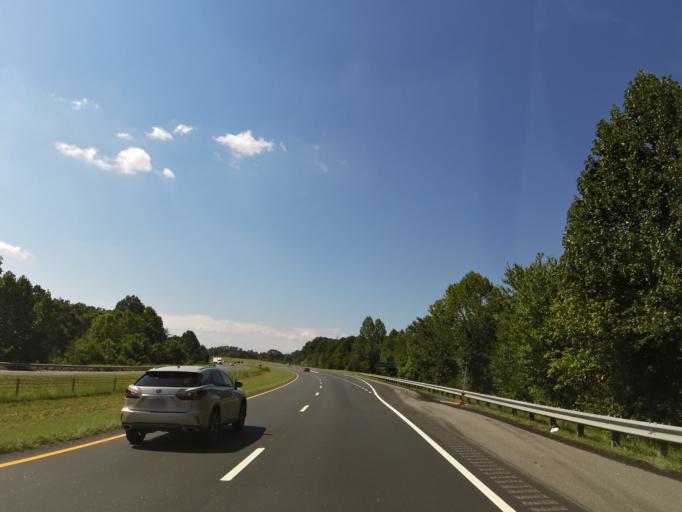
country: US
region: North Carolina
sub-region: Catawba County
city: Maiden
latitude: 35.5902
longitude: -81.2496
